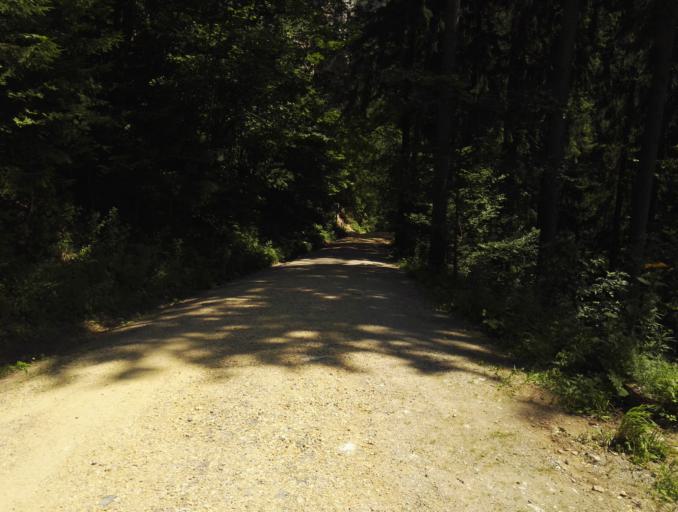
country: AT
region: Styria
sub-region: Politischer Bezirk Graz-Umgebung
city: Rothelstein
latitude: 47.3441
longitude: 15.3912
